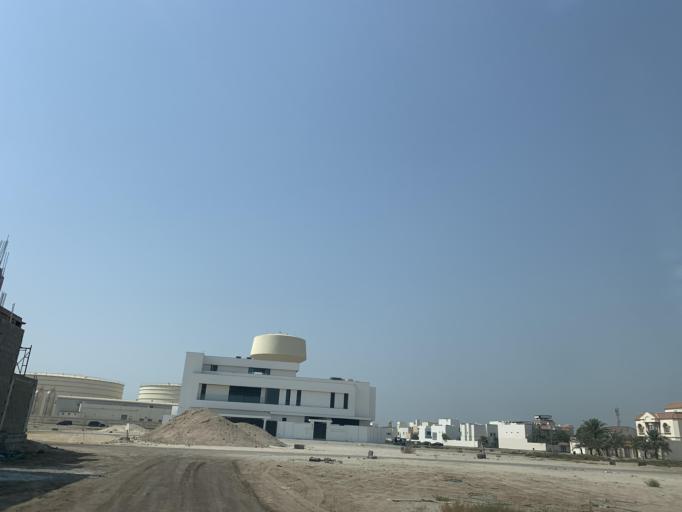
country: BH
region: Manama
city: Jidd Hafs
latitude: 26.2058
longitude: 50.5271
